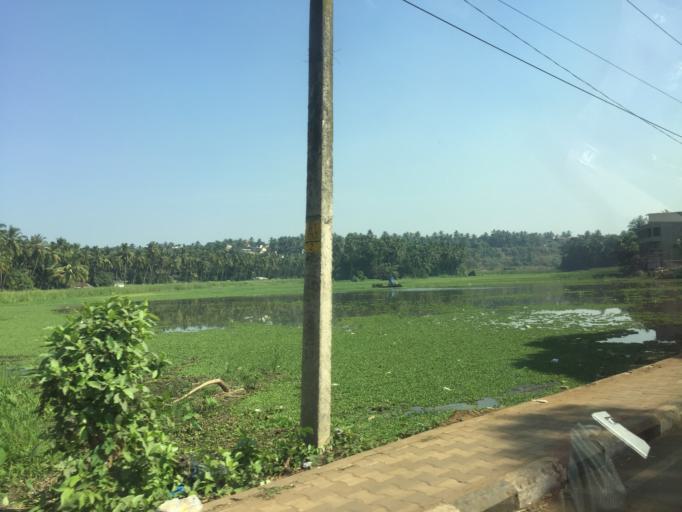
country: IN
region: Goa
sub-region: South Goa
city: Vasco Da Gama
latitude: 15.3976
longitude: 73.8180
